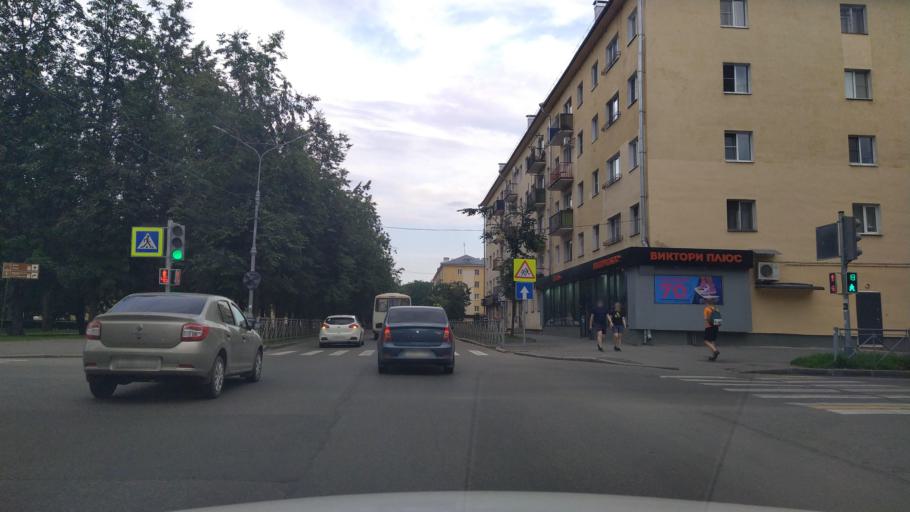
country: RU
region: Novgorod
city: Velikiy Novgorod
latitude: 58.5230
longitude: 31.2652
